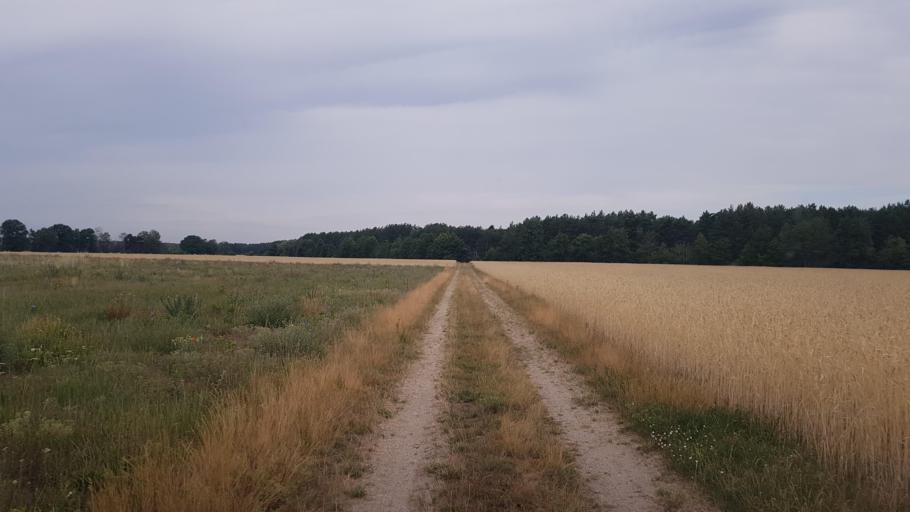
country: DE
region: Saxony-Anhalt
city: Holzdorf
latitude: 51.7597
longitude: 13.1859
